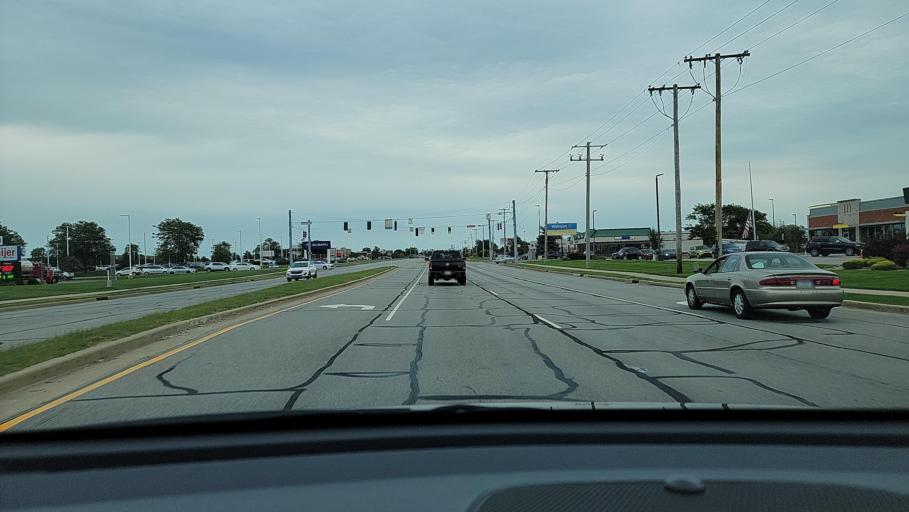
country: US
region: Indiana
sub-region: Porter County
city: Portage
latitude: 41.5505
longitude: -87.1808
